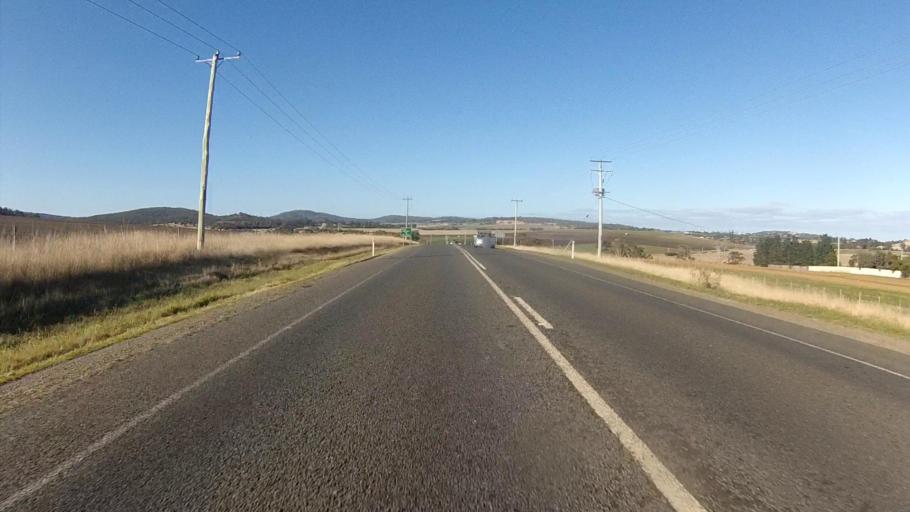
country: AU
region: Tasmania
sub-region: Sorell
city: Sorell
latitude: -42.7963
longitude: 147.6110
